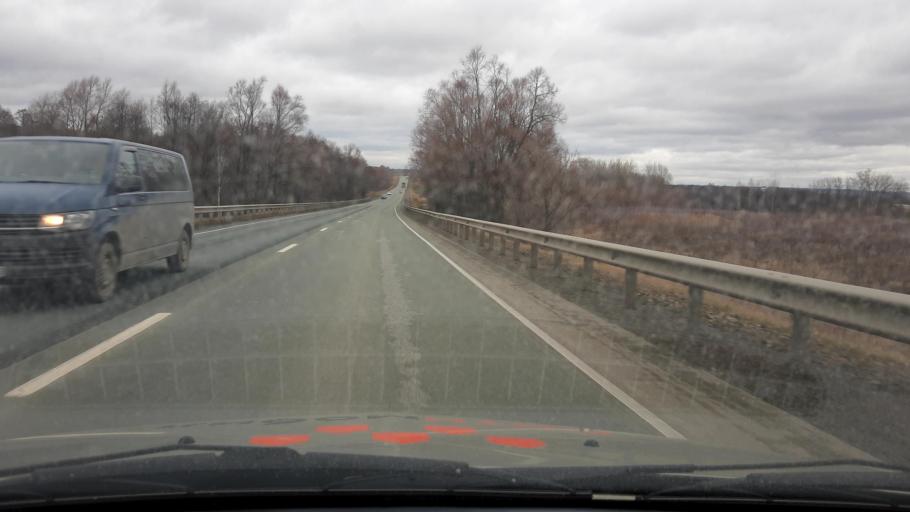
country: RU
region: Bashkortostan
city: Avdon
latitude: 54.7590
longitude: 55.7814
